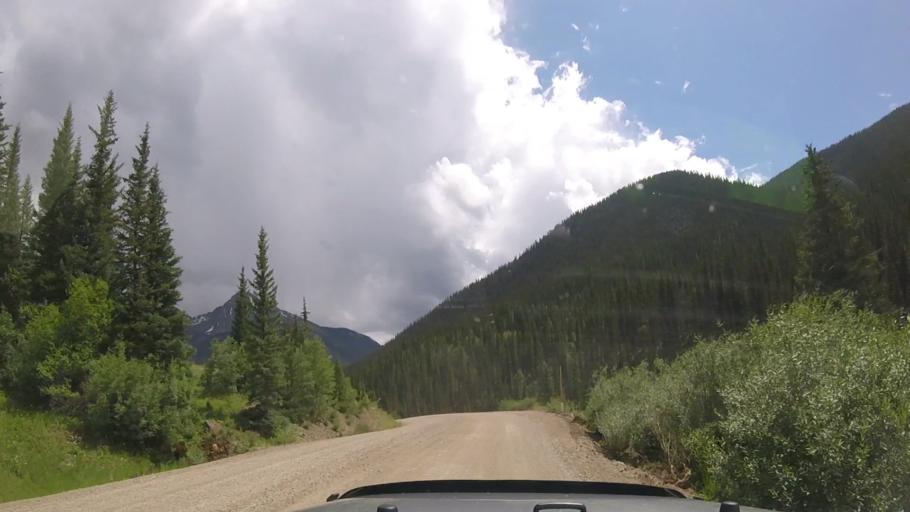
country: US
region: Colorado
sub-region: San Juan County
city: Silverton
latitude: 37.8278
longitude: -107.6692
